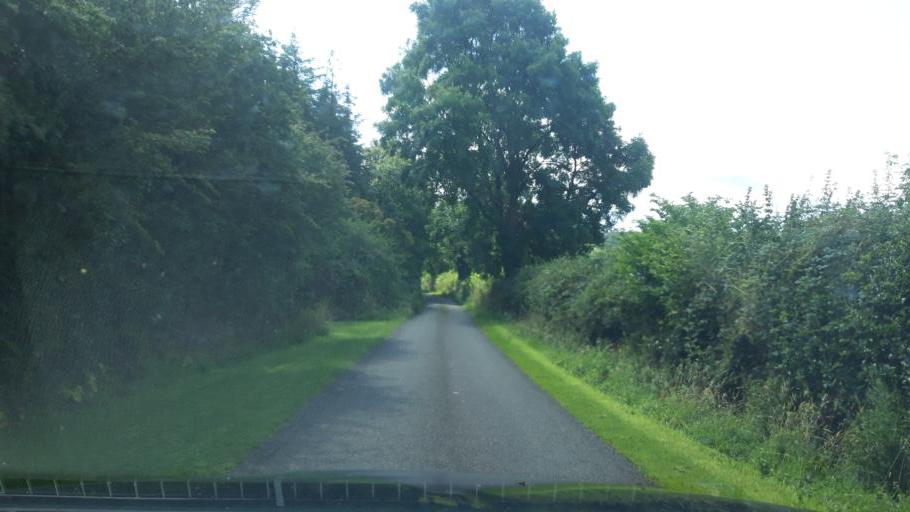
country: IE
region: Leinster
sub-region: Kilkenny
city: Graiguenamanagh
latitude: 52.5810
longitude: -6.9900
